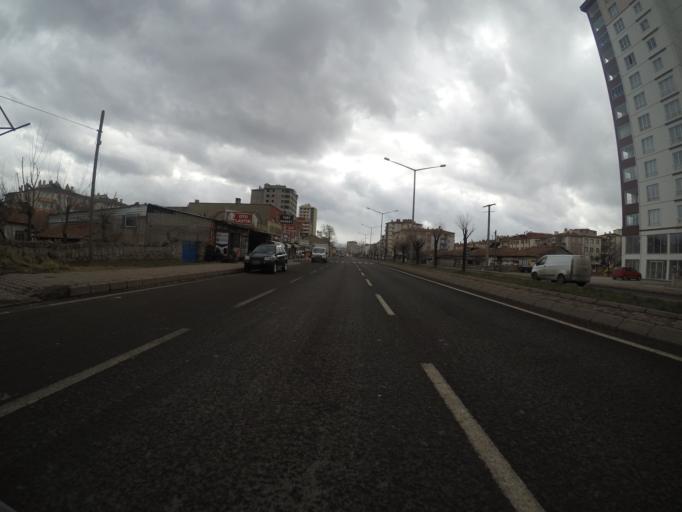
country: TR
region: Kayseri
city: Melikgazi
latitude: 38.7593
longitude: 35.4664
